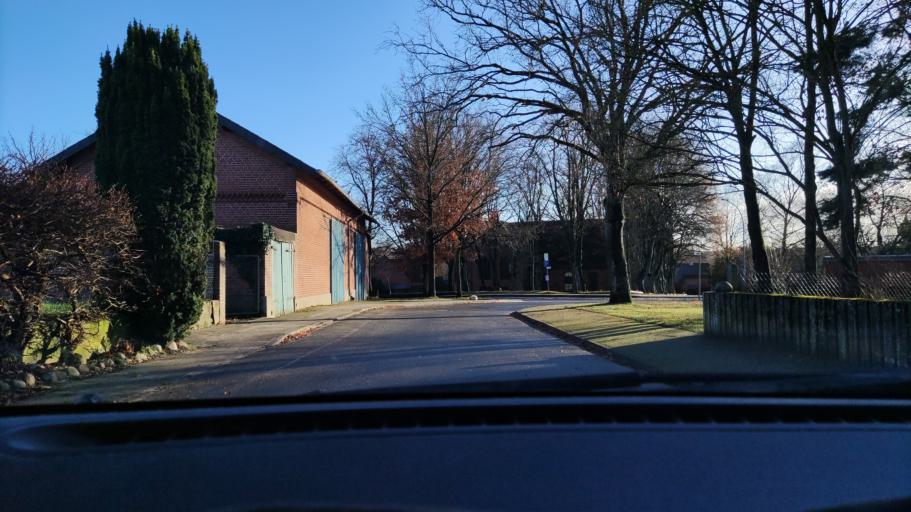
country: DE
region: Lower Saxony
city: Gerdau
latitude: 52.9686
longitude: 10.4185
